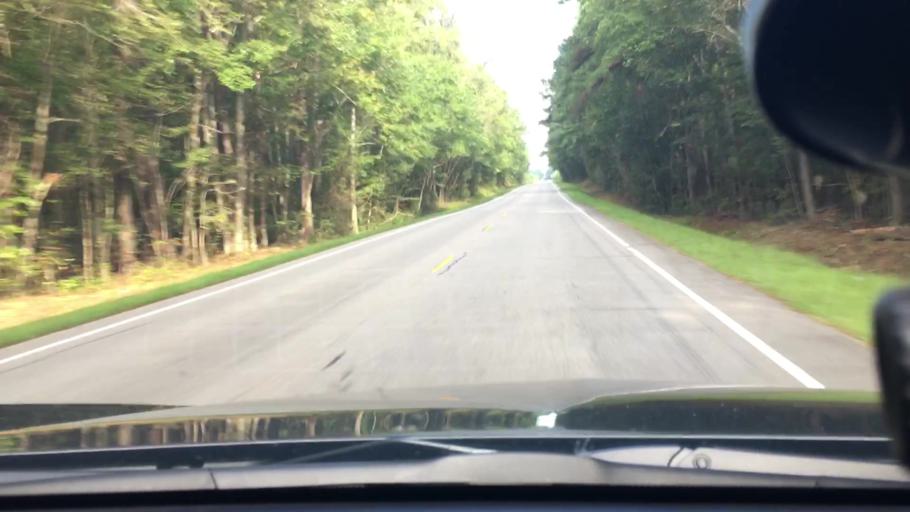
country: US
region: North Carolina
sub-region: Edgecombe County
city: Pinetops
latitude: 35.7665
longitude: -77.5650
